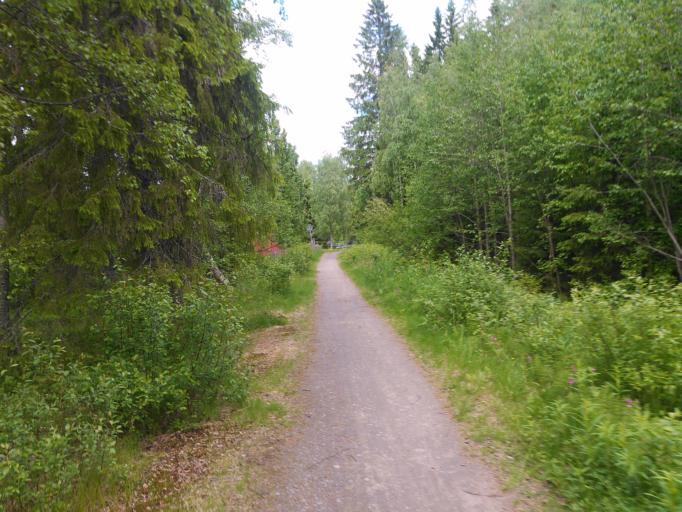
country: SE
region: Vaesterbotten
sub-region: Umea Kommun
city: Ersmark
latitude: 63.8684
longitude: 20.3341
